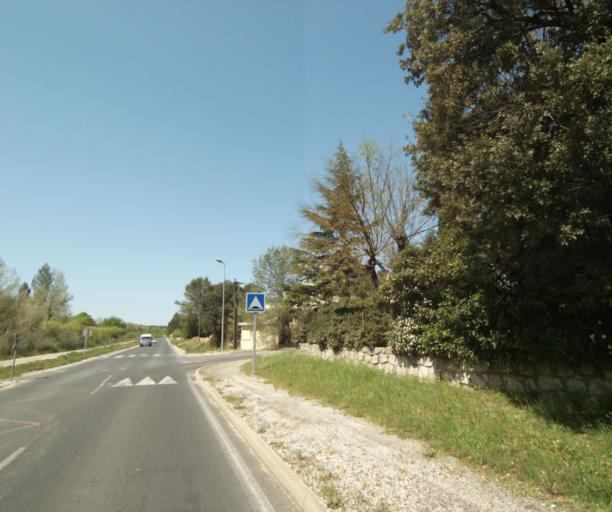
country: FR
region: Languedoc-Roussillon
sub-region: Departement de l'Herault
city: Montferrier-sur-Lez
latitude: 43.6588
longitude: 3.8504
